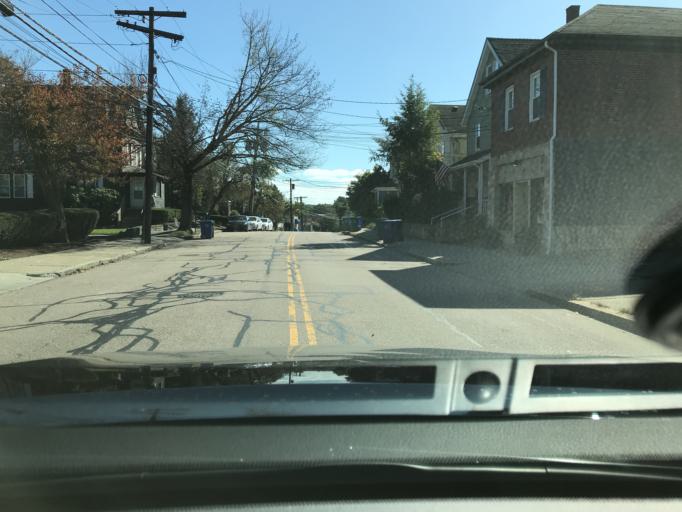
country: US
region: Massachusetts
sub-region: Middlesex County
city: Newton
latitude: 42.3209
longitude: -71.1837
